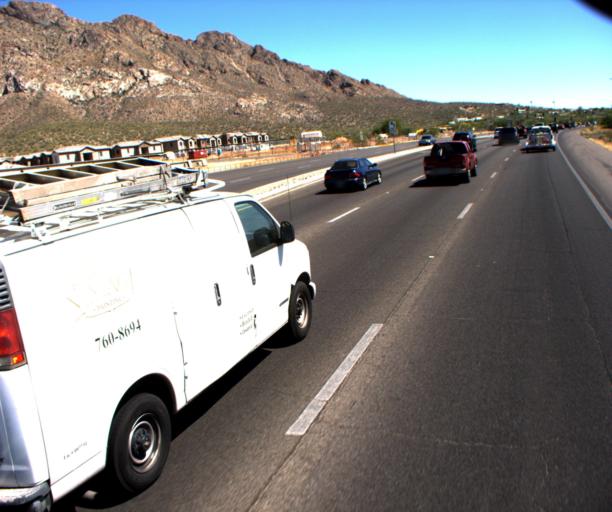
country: US
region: Arizona
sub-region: Pima County
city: Oro Valley
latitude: 32.3838
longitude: -110.9641
